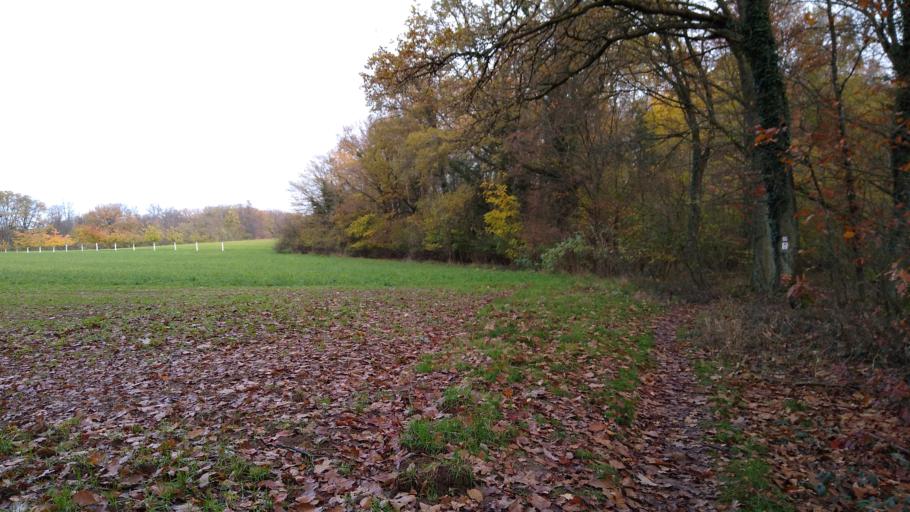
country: DE
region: Bavaria
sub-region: Regierungsbezirk Mittelfranken
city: Kalchreuth
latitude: 49.5458
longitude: 11.1158
